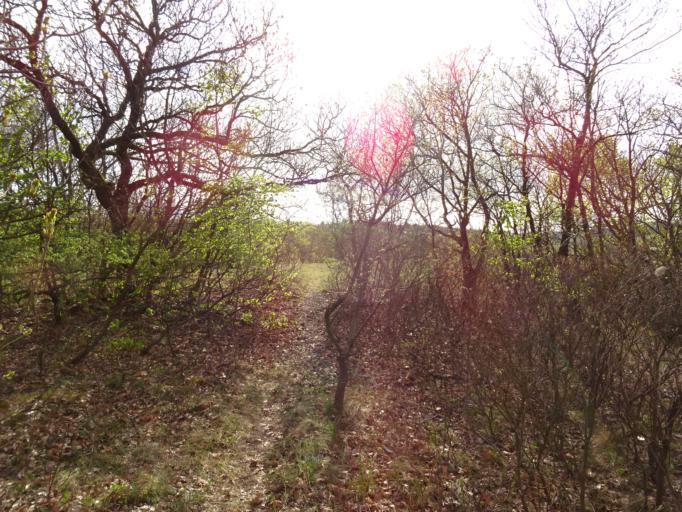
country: HU
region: Veszprem
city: Varpalota
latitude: 47.2264
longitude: 18.0971
